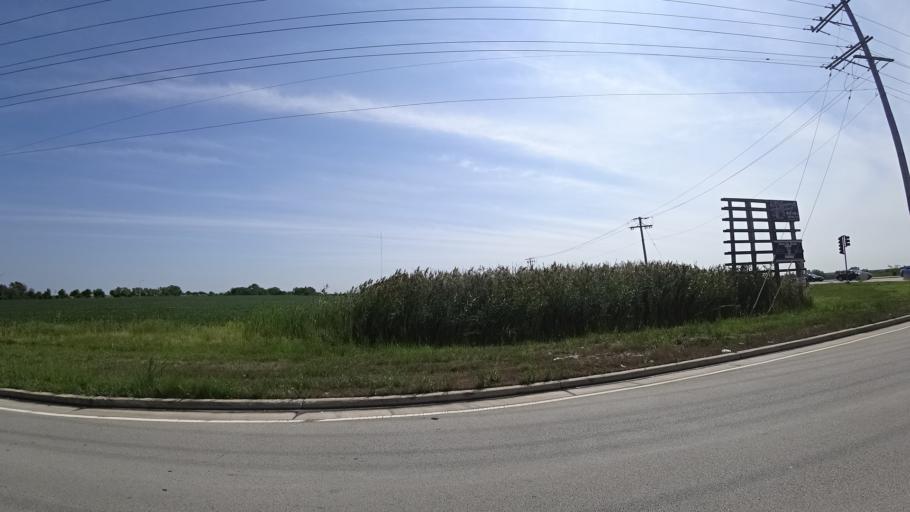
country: US
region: Illinois
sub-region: Cook County
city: Orland Hills
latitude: 41.5649
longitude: -87.8510
